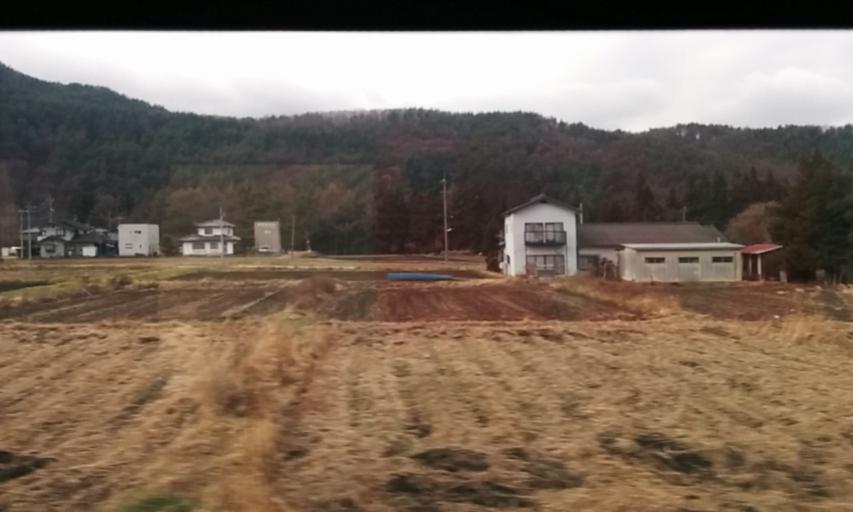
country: JP
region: Nagano
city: Shiojiri
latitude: 36.0792
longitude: 137.9089
